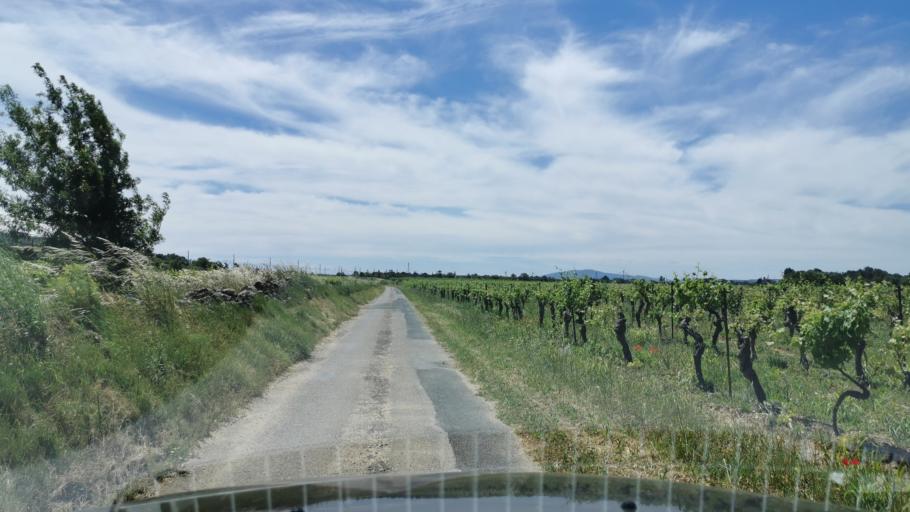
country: FR
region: Languedoc-Roussillon
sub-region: Departement de l'Aude
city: Nevian
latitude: 43.2153
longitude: 2.8850
